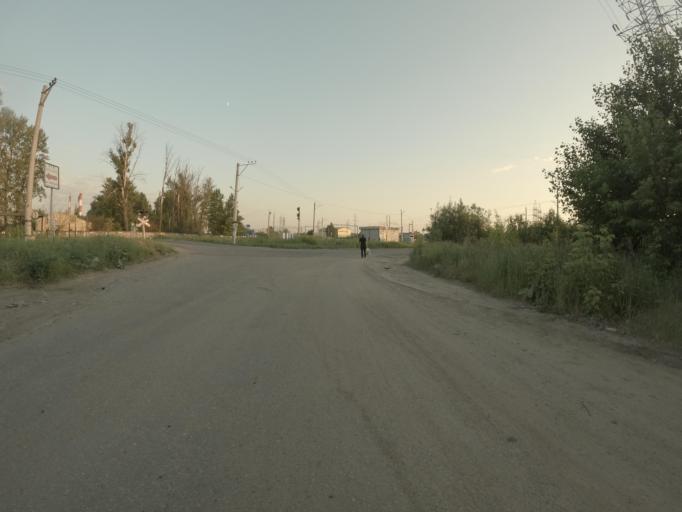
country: RU
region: St.-Petersburg
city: Avtovo
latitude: 59.8791
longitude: 30.2844
